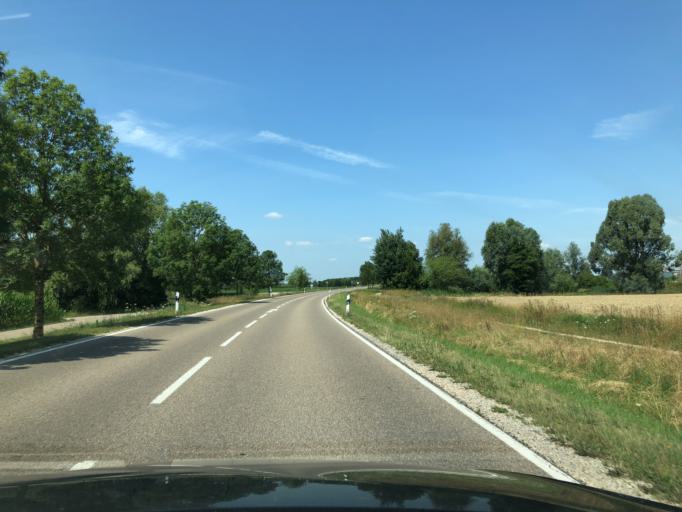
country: DE
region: Bavaria
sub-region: Swabia
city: Mertingen
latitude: 48.6474
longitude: 10.8015
